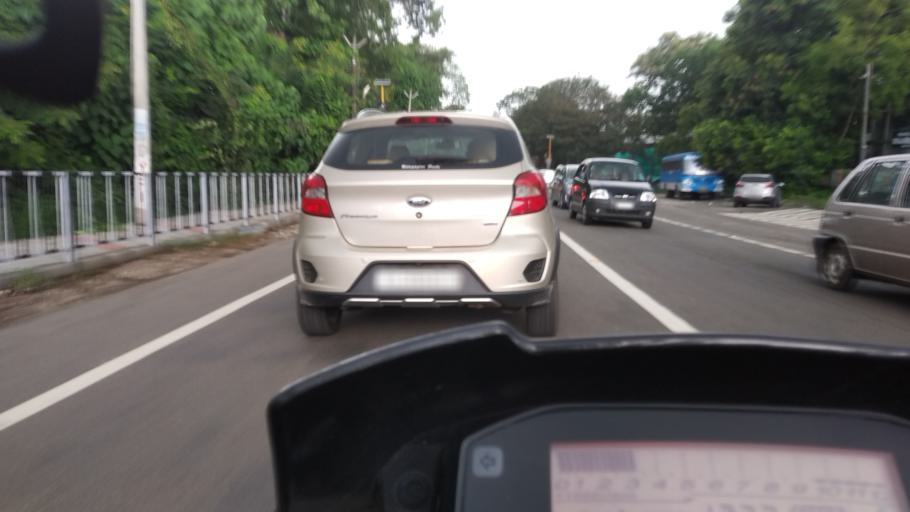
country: IN
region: Kerala
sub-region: Thiruvananthapuram
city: Attingal
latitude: 8.7075
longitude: 76.8147
